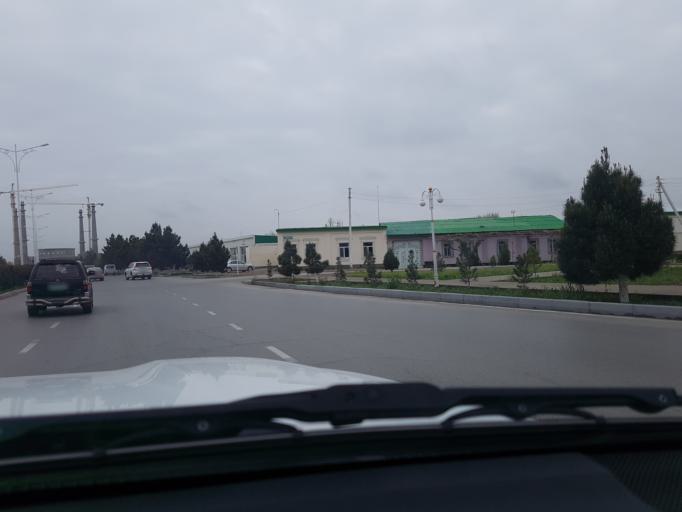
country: TM
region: Lebap
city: Turkmenabat
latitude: 39.0329
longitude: 63.5889
